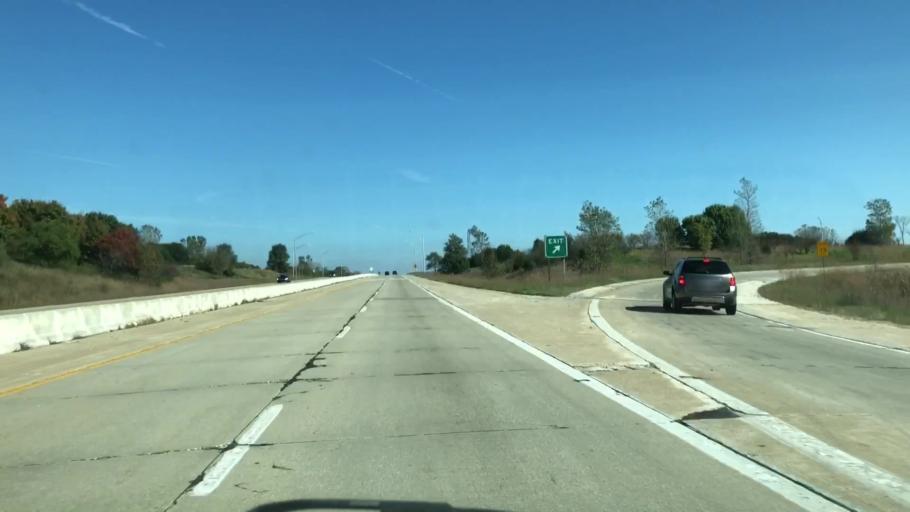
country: US
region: Indiana
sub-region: Elkhart County
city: Elkhart
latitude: 41.6316
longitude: -86.0011
